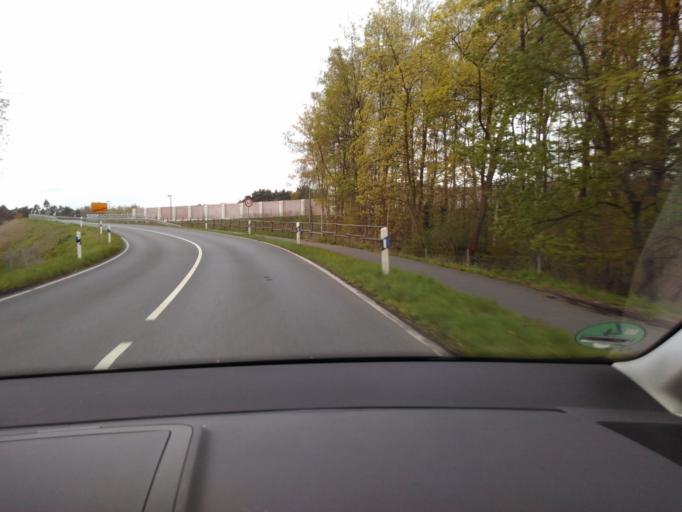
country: DE
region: North Rhine-Westphalia
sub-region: Regierungsbezirk Detmold
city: Bielefeld
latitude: 51.9619
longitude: 8.5025
